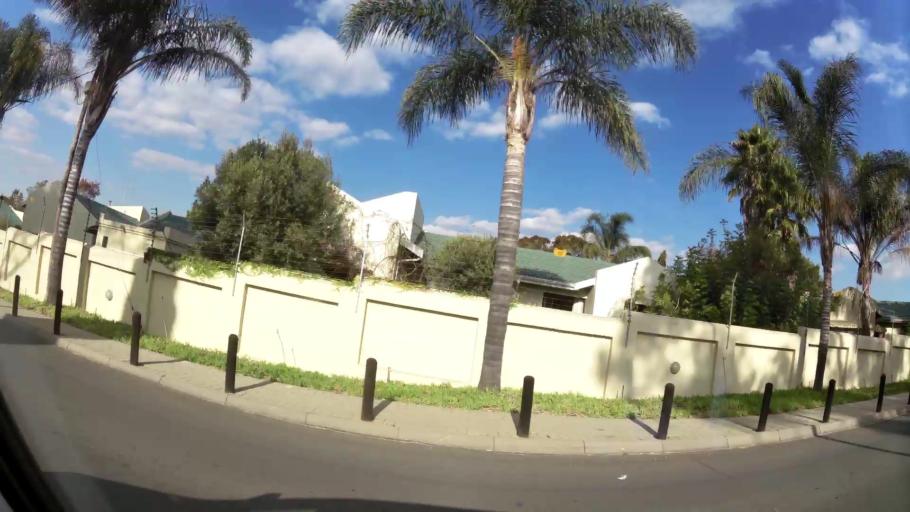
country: ZA
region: Gauteng
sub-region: City of Johannesburg Metropolitan Municipality
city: Diepsloot
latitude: -26.0083
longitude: 28.0174
